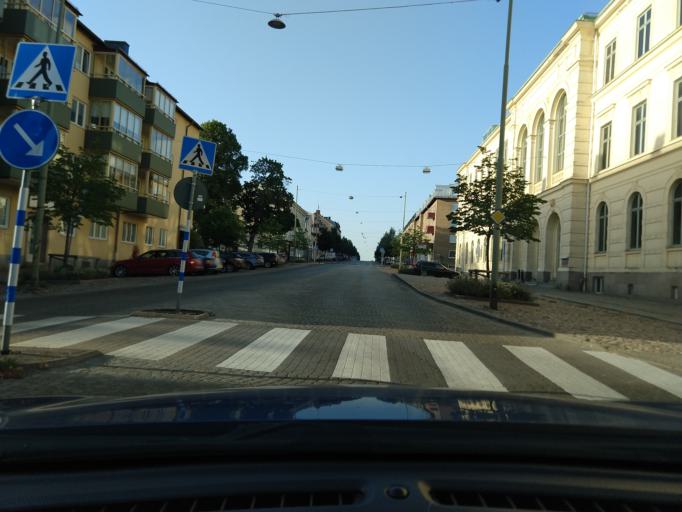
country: SE
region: Blekinge
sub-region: Karlskrona Kommun
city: Karlskrona
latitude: 56.1643
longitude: 15.5915
